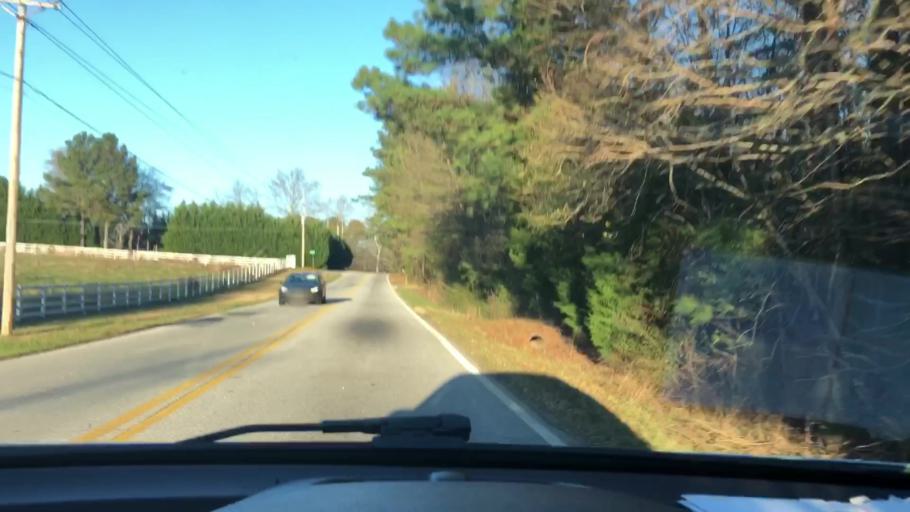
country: US
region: Georgia
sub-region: Rockdale County
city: Lakeview Estates
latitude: 33.7463
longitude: -84.0330
